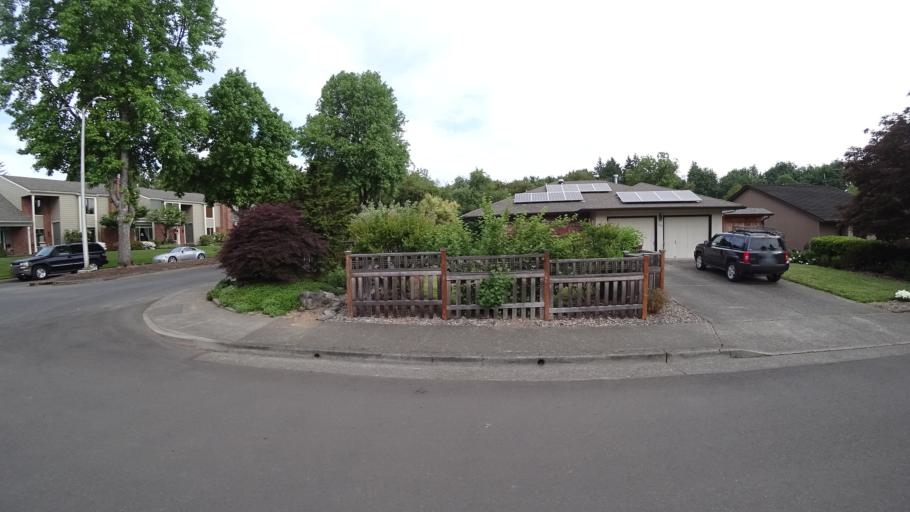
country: US
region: Oregon
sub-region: Clackamas County
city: Lake Oswego
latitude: 45.4323
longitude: -122.6785
